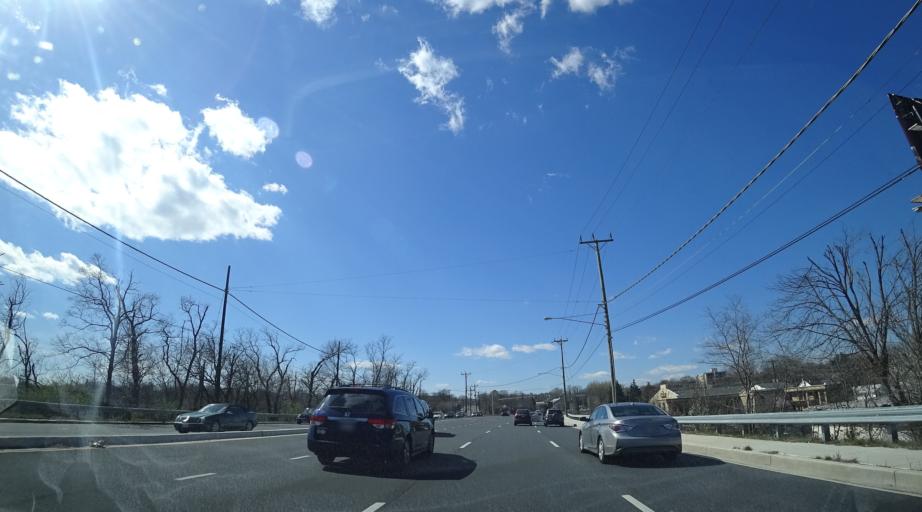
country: US
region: Maryland
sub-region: Prince George's County
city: Berwyn Heights
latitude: 38.9981
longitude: -76.9217
